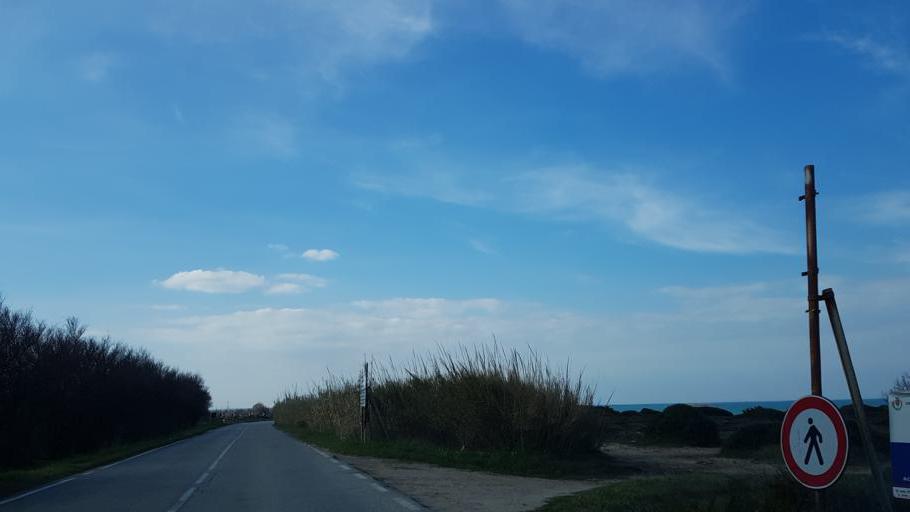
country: IT
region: Apulia
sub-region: Provincia di Brindisi
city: Brindisi
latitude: 40.6897
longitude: 17.8414
